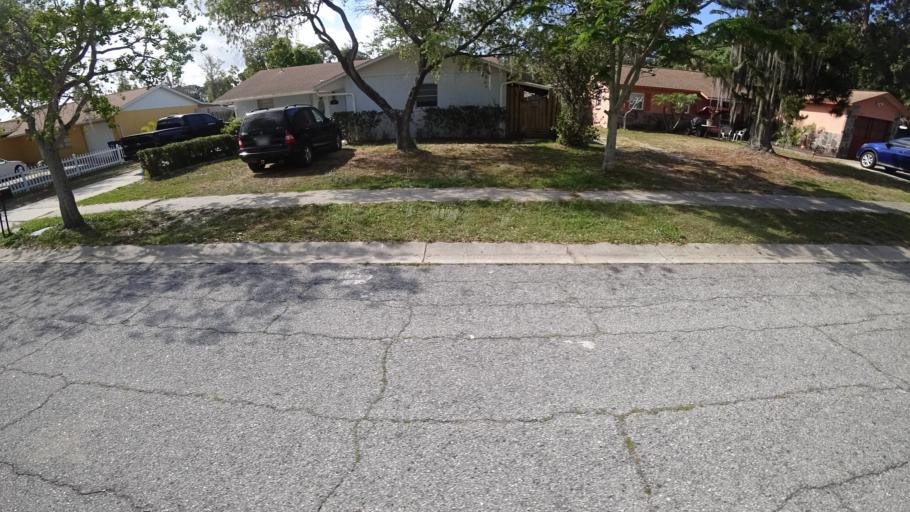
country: US
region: Florida
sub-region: Manatee County
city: Whitfield
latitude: 27.4246
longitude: -82.5713
